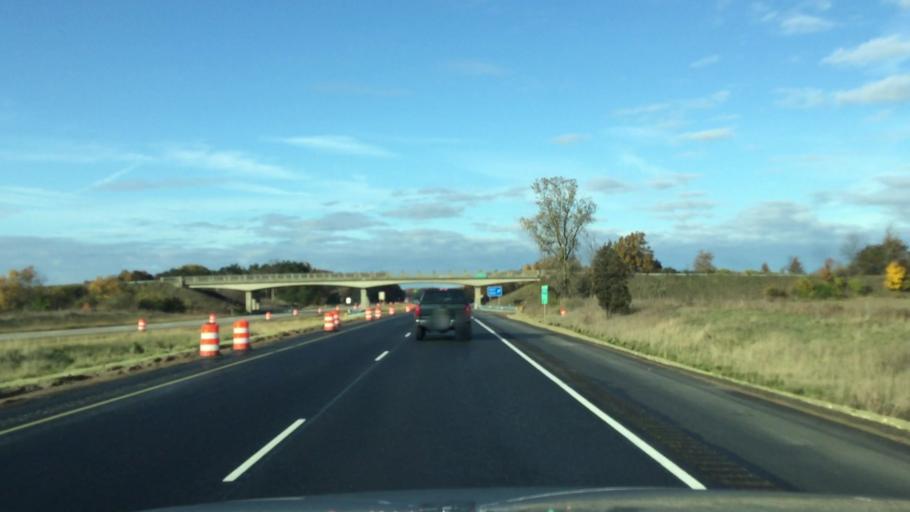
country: US
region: Michigan
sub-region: Calhoun County
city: Marshall
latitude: 42.2829
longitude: -84.9048
